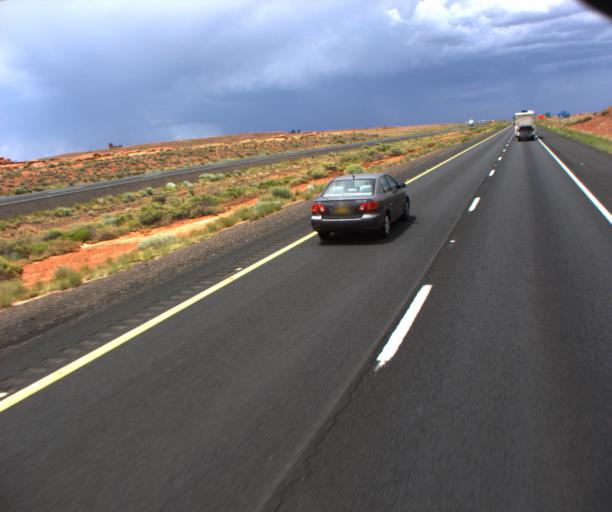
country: US
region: Arizona
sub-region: Coconino County
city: LeChee
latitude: 35.1073
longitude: -111.0121
